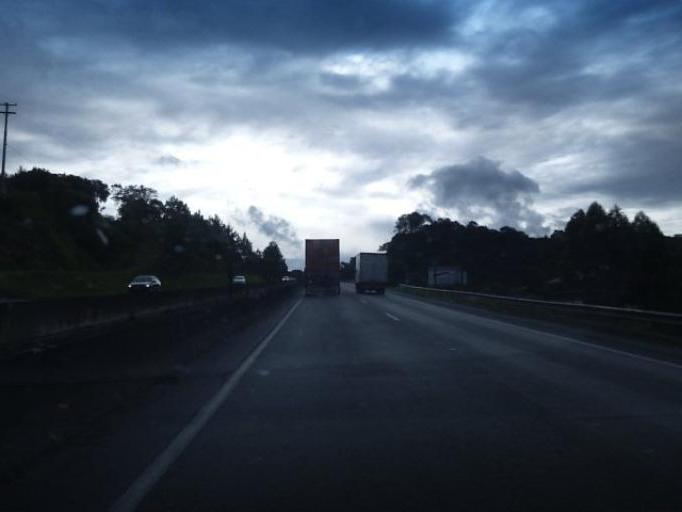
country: BR
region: Parana
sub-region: Campina Grande Do Sul
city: Campina Grande do Sul
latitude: -25.3063
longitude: -48.9754
